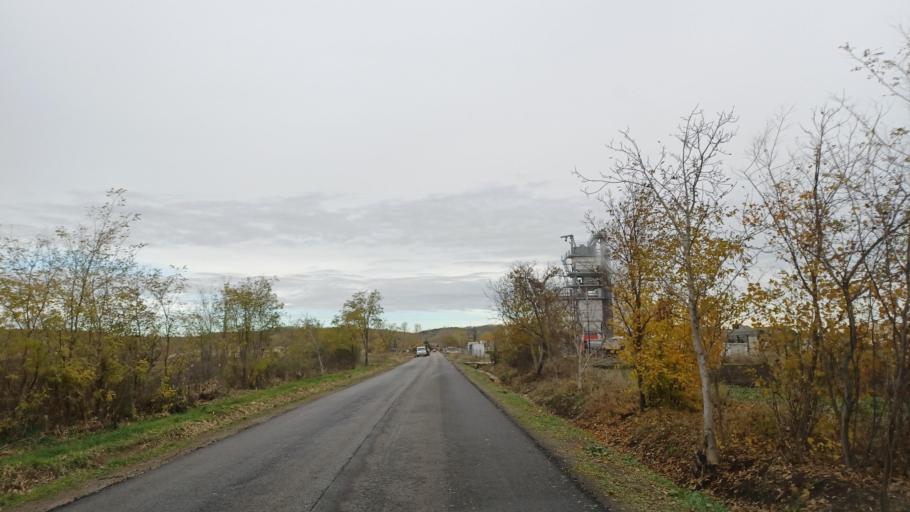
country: HU
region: Tolna
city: Dunaszentgyorgy
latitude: 46.5224
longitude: 18.7734
